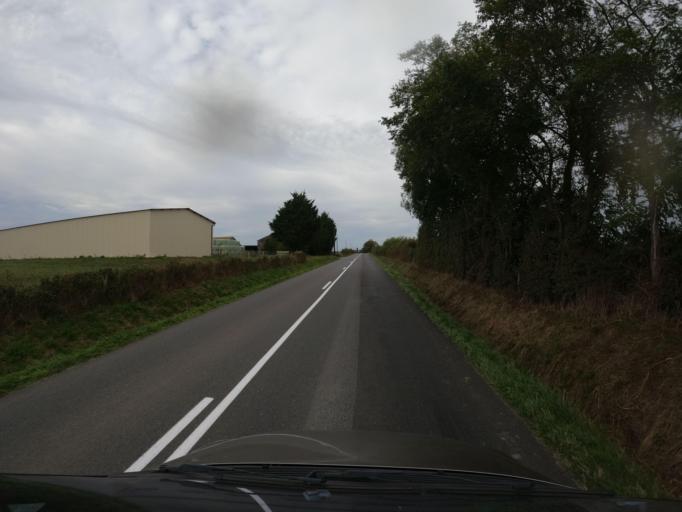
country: FR
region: Poitou-Charentes
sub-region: Departement de la Vienne
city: Saulge
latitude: 46.3825
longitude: 0.8478
